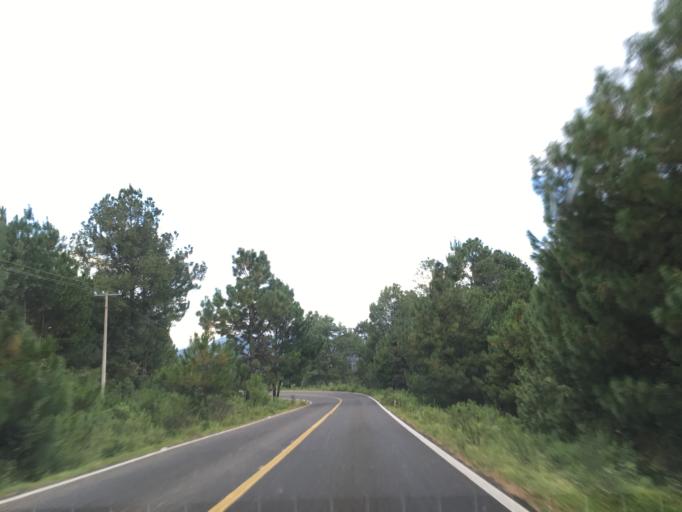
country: MX
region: Michoacan
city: Pichataro
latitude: 19.5889
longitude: -101.8317
